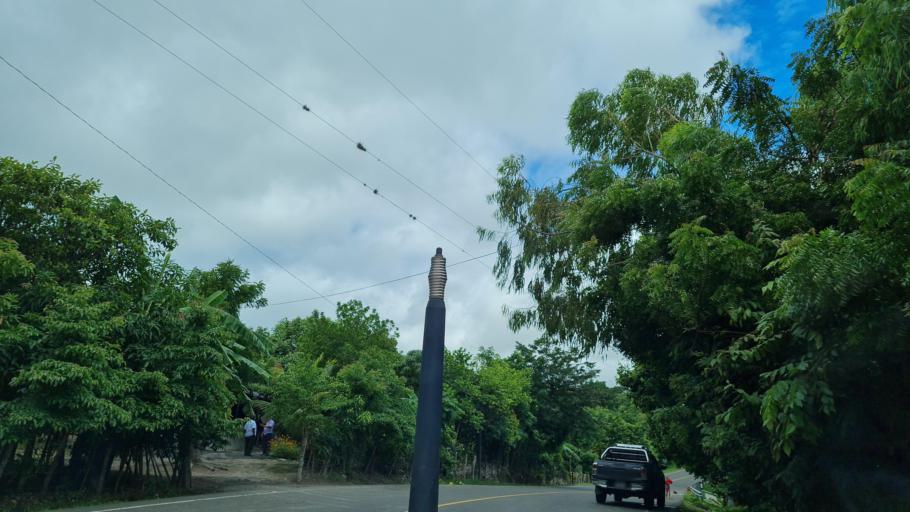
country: NI
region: Boaco
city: San Jose de los Remates
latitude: 12.5914
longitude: -85.9042
